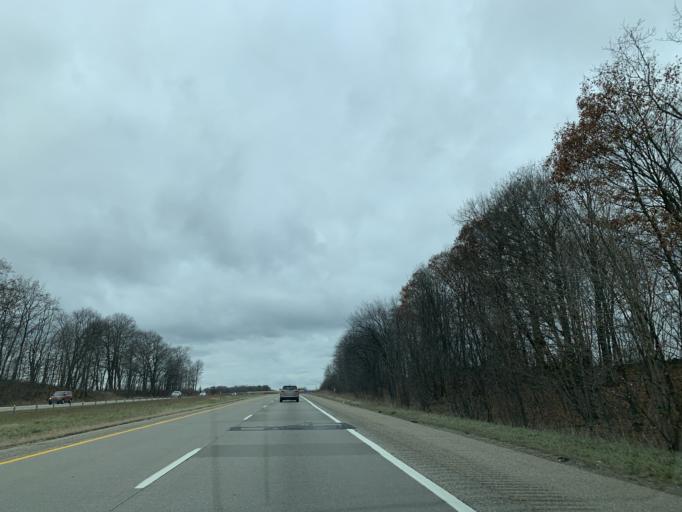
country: US
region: Michigan
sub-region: Kent County
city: Lowell
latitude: 42.8787
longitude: -85.4019
